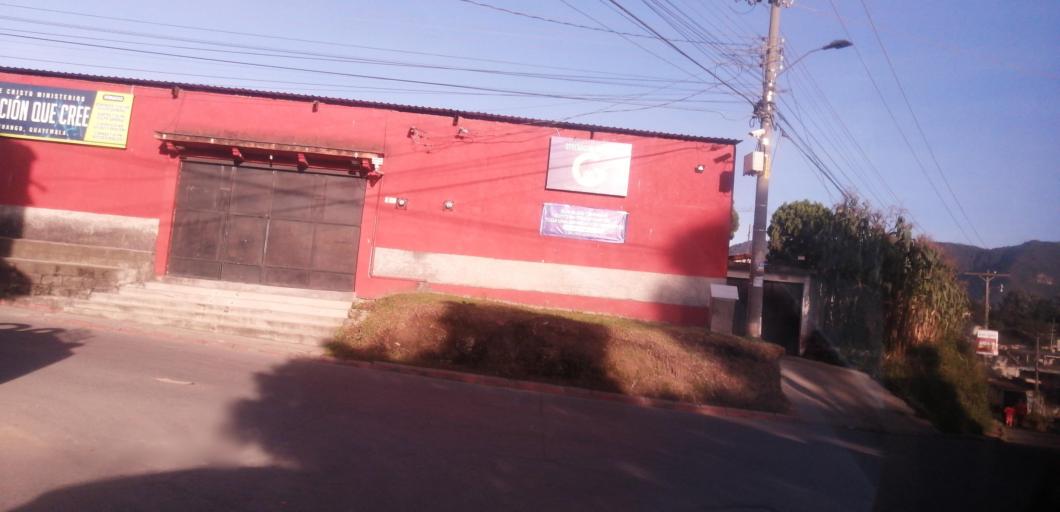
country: GT
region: Quetzaltenango
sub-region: Municipio de La Esperanza
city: La Esperanza
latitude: 14.8651
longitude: -91.5389
